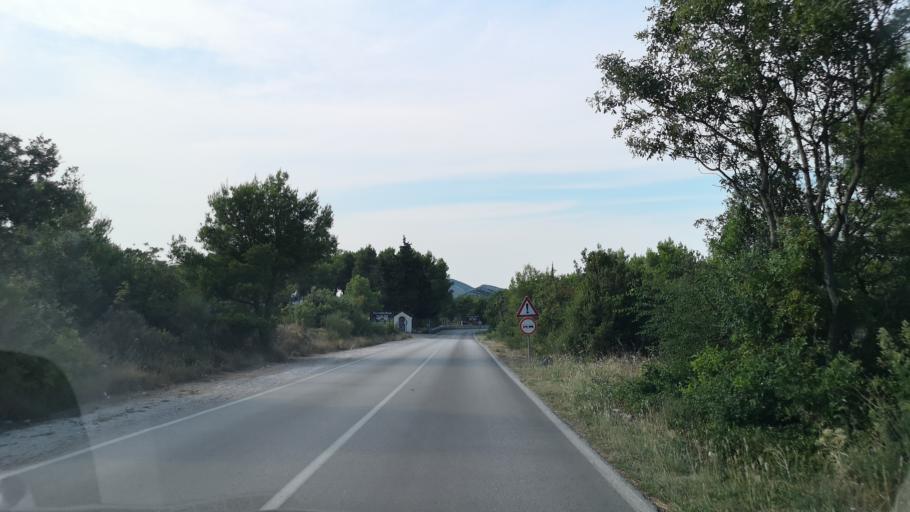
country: HR
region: Sibensko-Kniniska
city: Vodice
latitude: 43.7873
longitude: 15.7705
